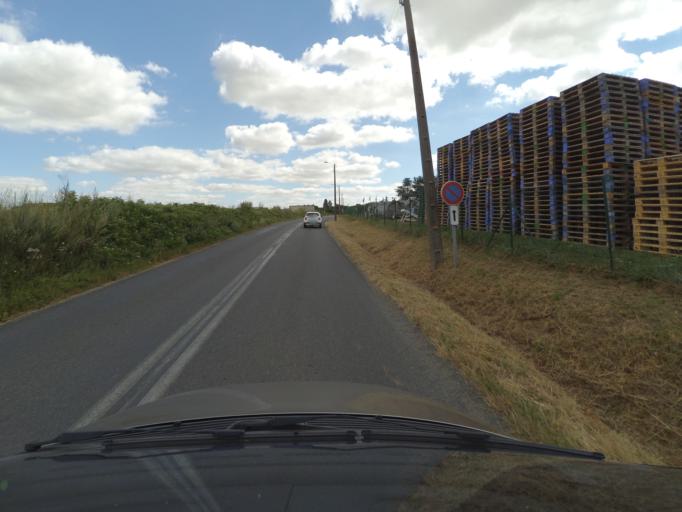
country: FR
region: Pays de la Loire
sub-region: Departement de Maine-et-Loire
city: Doue-la-Fontaine
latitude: 47.2043
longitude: -0.2762
